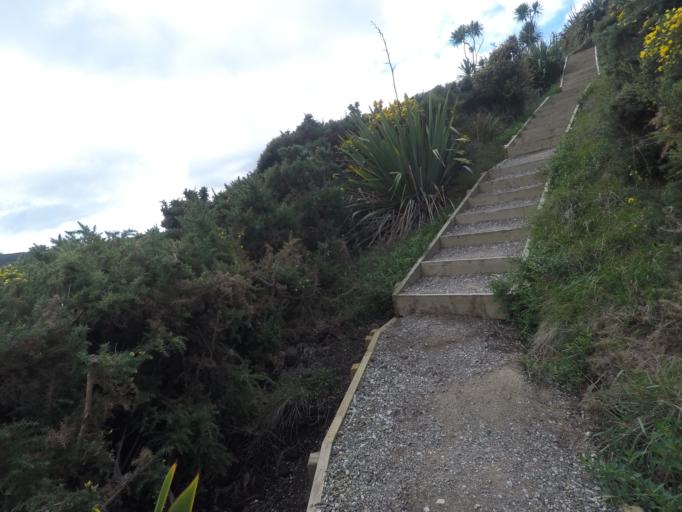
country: NZ
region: Auckland
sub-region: Auckland
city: Titirangi
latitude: -37.0413
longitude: 174.5117
